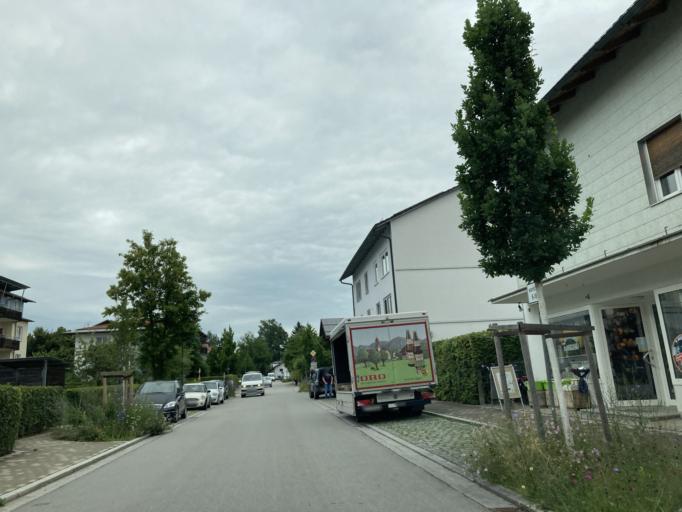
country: DE
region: Bavaria
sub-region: Upper Bavaria
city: Stephanskirchen
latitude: 47.8597
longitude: 12.1713
